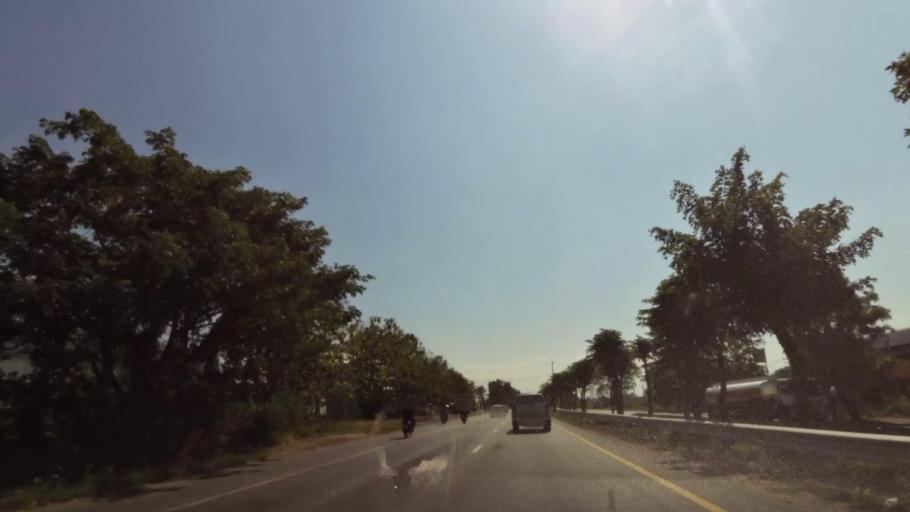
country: TH
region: Nakhon Sawan
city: Kao Liao
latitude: 15.8036
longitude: 100.1201
